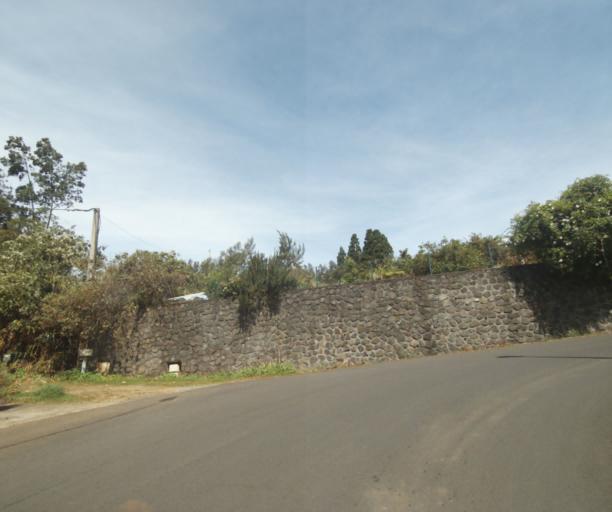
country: RE
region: Reunion
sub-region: Reunion
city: Trois-Bassins
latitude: -21.0482
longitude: 55.3400
